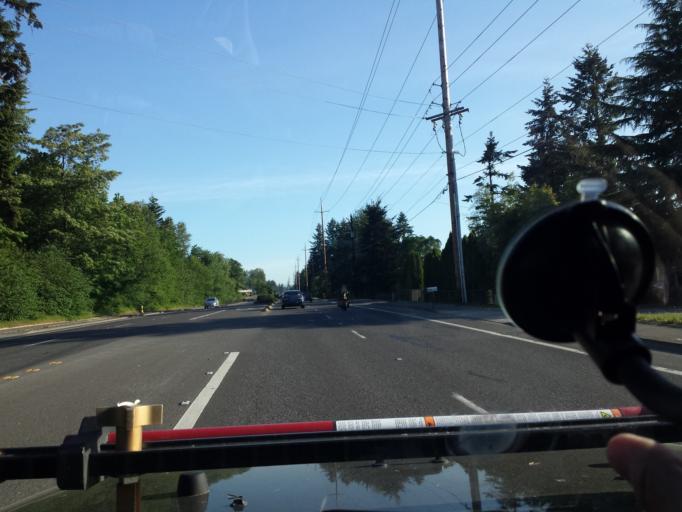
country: US
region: Washington
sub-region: Clark County
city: Mill Plain
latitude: 45.6660
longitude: -122.5059
